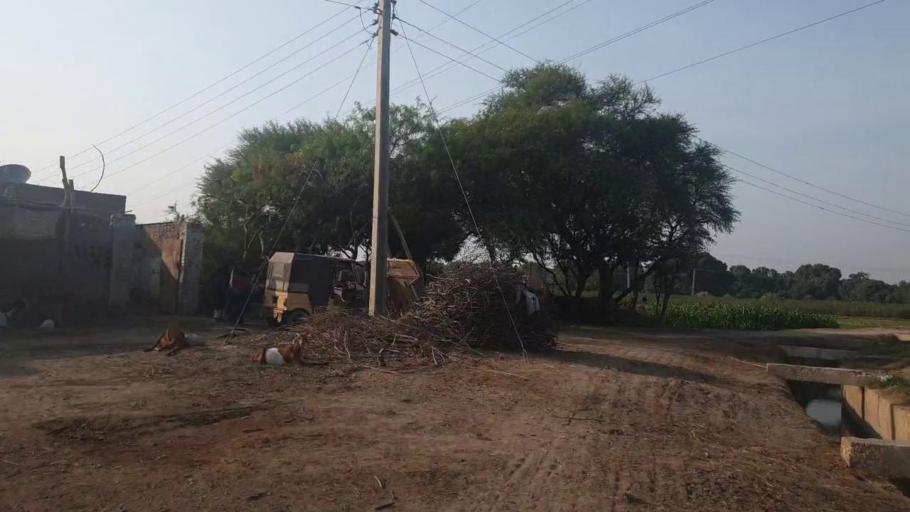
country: PK
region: Sindh
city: Tando Jam
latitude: 25.4267
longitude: 68.4651
